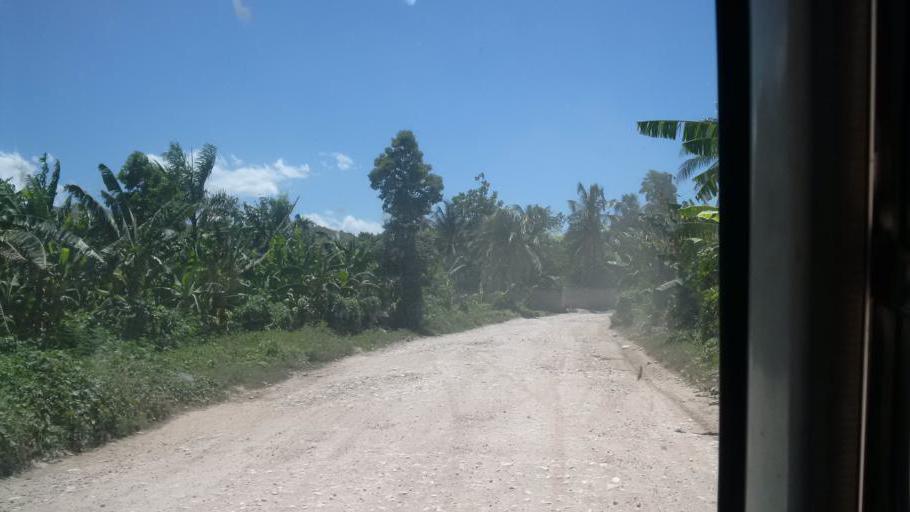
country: HT
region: Ouest
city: Thomazeau
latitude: 18.6571
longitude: -72.1386
